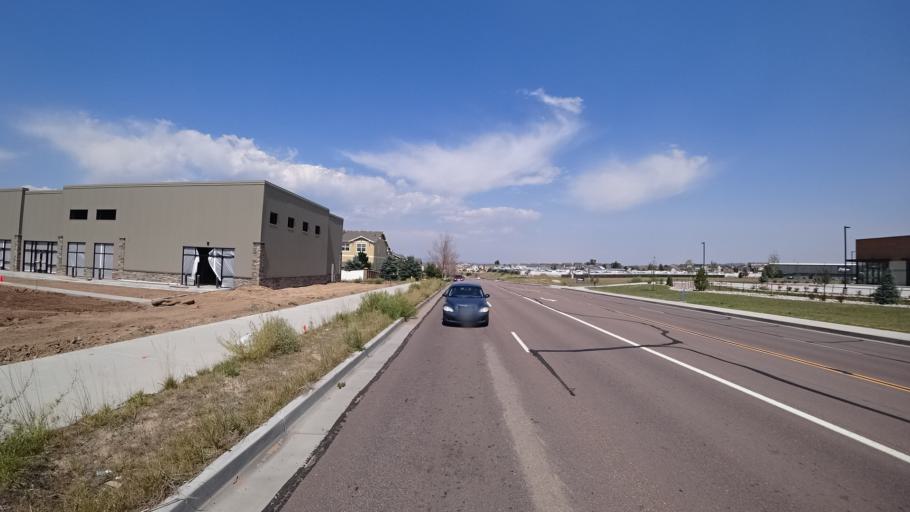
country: US
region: Colorado
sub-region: El Paso County
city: Cimarron Hills
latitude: 38.9270
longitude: -104.7224
